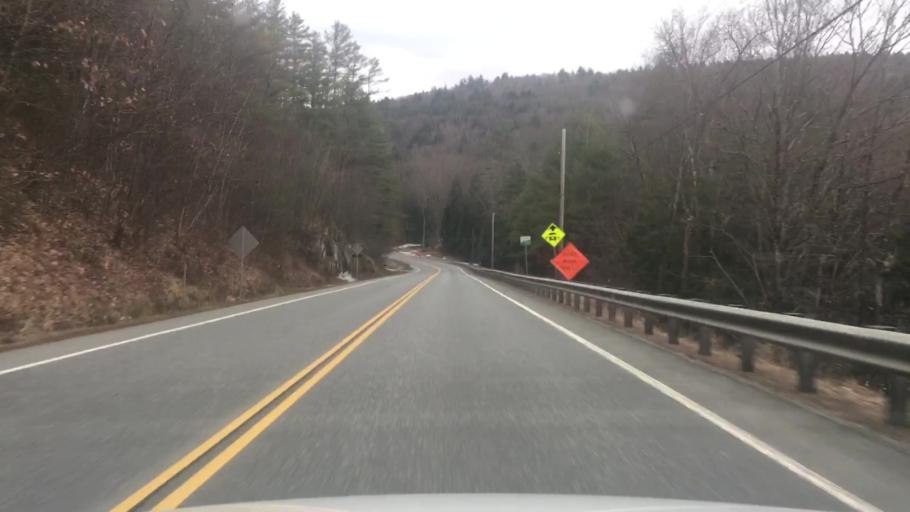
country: US
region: New Hampshire
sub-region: Cheshire County
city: Westmoreland
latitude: 42.9912
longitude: -72.4306
